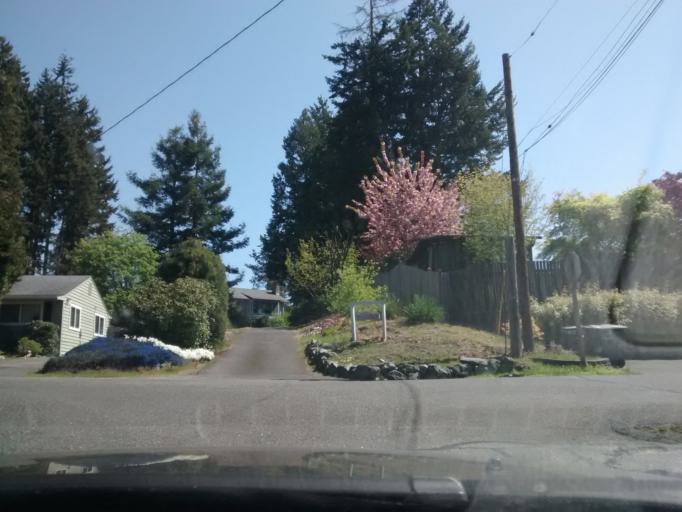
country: US
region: Washington
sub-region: Snohomish County
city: Esperance
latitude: 47.8106
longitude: -122.3442
